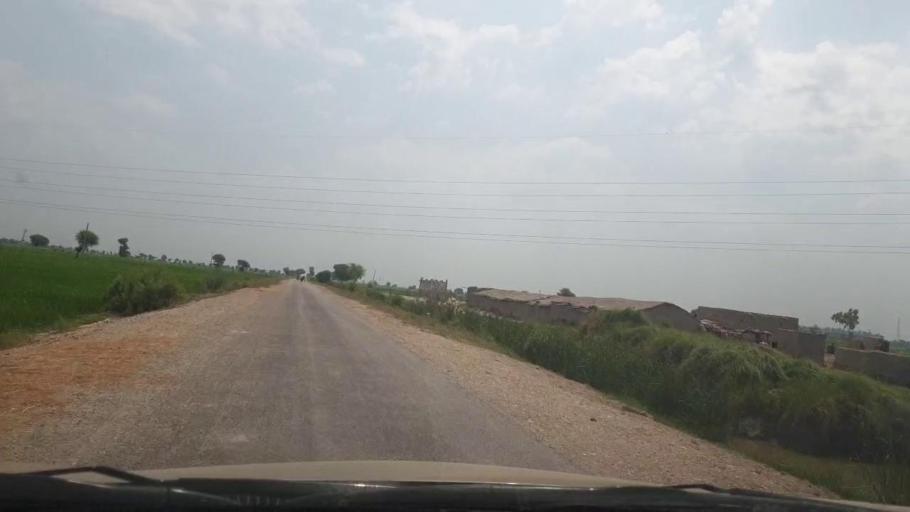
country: PK
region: Sindh
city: Ratodero
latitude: 27.7022
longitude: 68.2533
